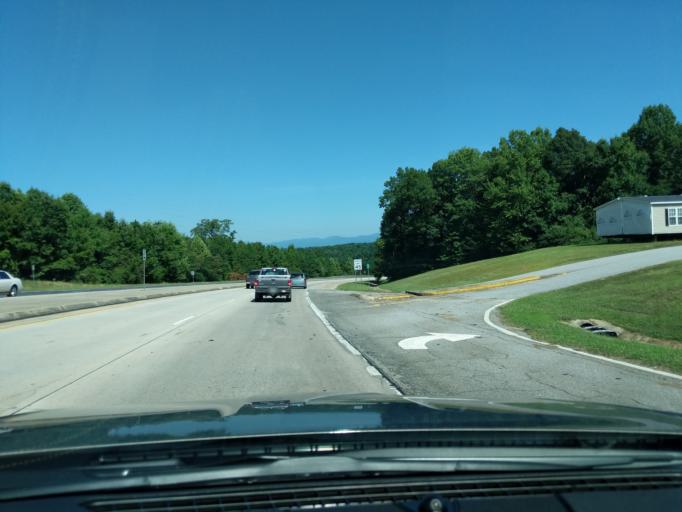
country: US
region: Georgia
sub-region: Habersham County
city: Baldwin
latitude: 34.5013
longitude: -83.5441
